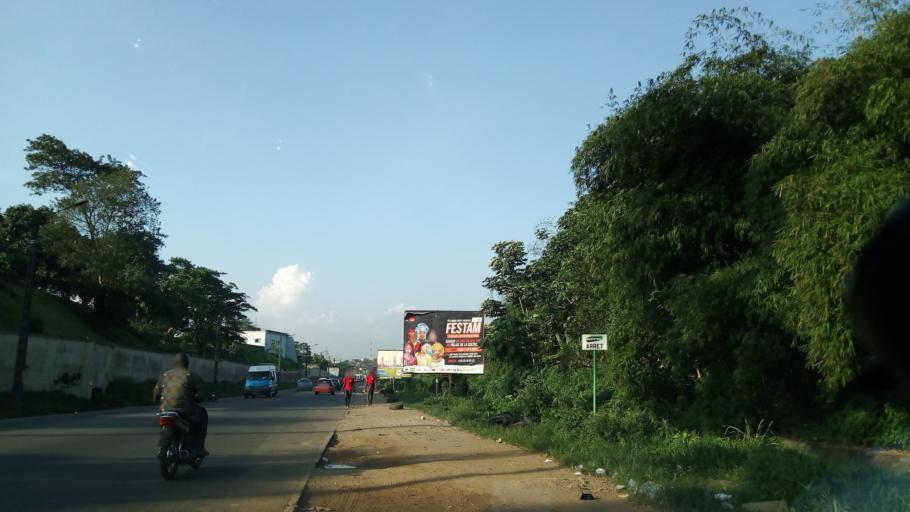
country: CI
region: Lagunes
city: Abobo
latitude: 5.3803
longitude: -4.0067
